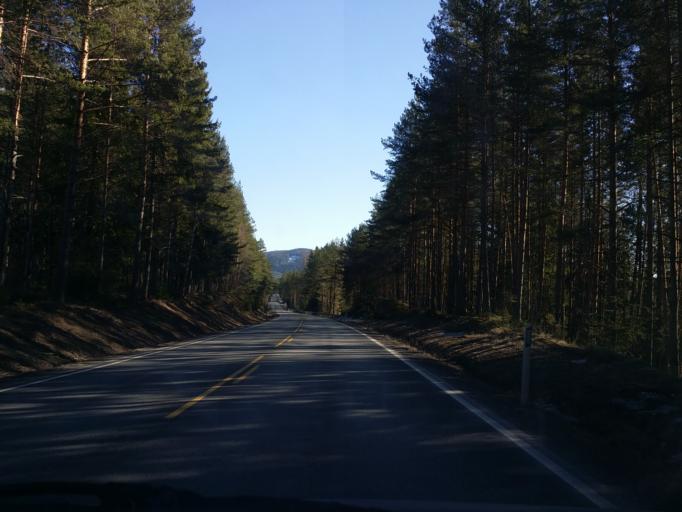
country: NO
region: Buskerud
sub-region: Ringerike
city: Honefoss
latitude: 60.3055
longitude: 10.1642
